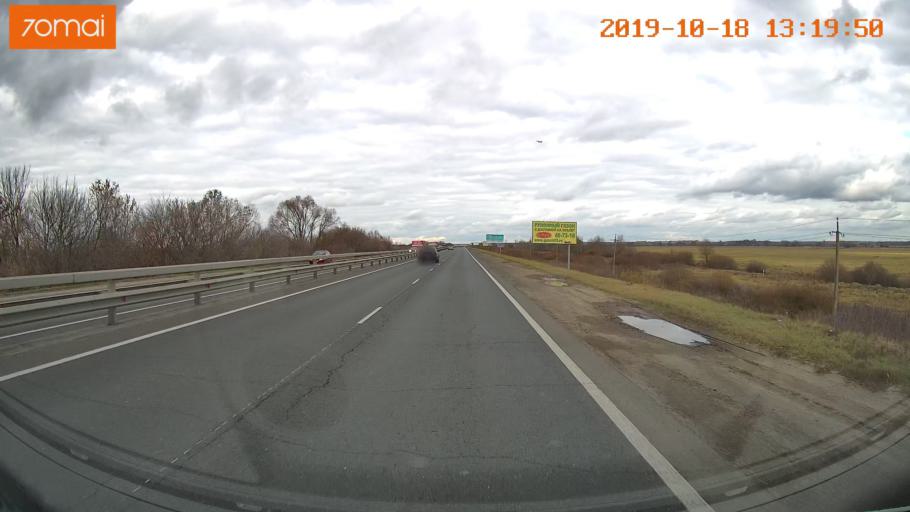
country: RU
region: Rjazan
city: Polyany
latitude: 54.6724
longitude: 39.8275
